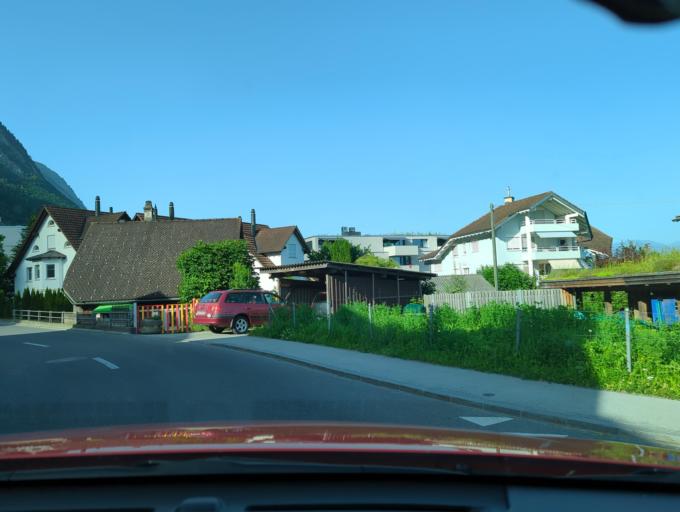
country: CH
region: Saint Gallen
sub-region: Wahlkreis Werdenberg
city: Sennwald
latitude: 47.2454
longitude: 9.4743
